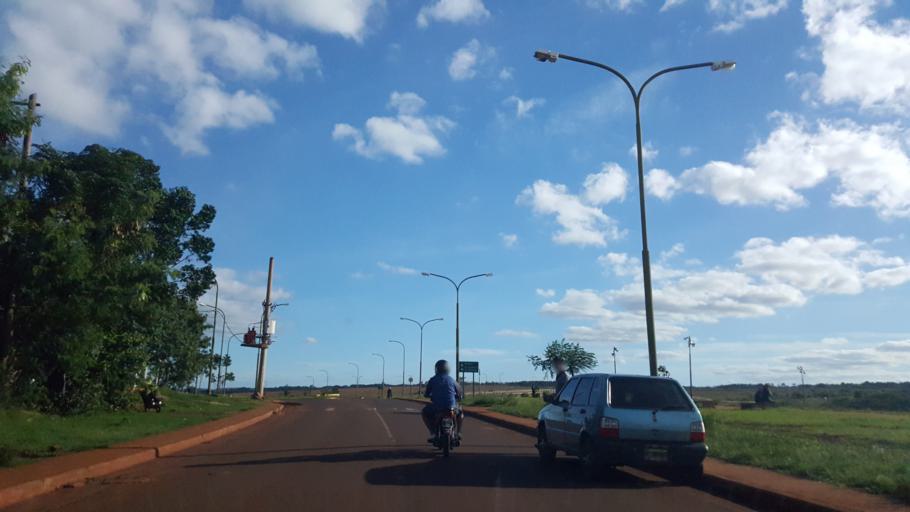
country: AR
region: Misiones
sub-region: Departamento de Capital
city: Posadas
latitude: -27.3796
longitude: -55.9522
